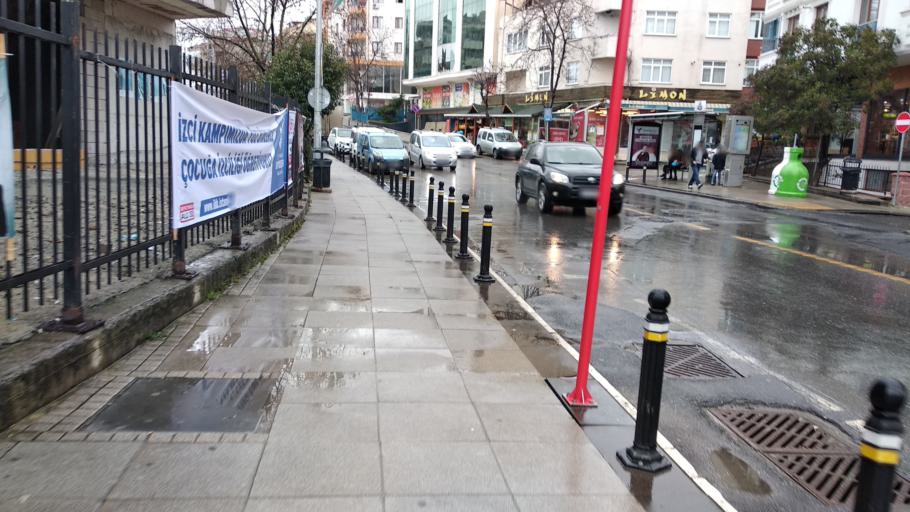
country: TR
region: Istanbul
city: Samandira
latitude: 41.0256
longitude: 29.1813
